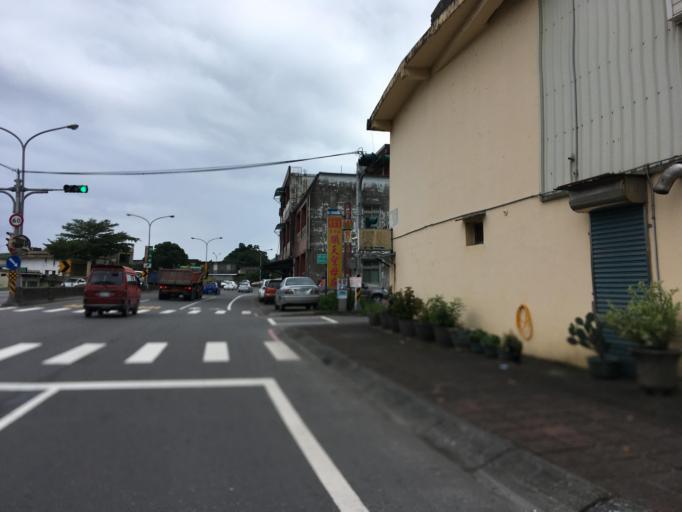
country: TW
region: Taiwan
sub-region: Yilan
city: Yilan
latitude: 24.6154
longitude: 121.8211
